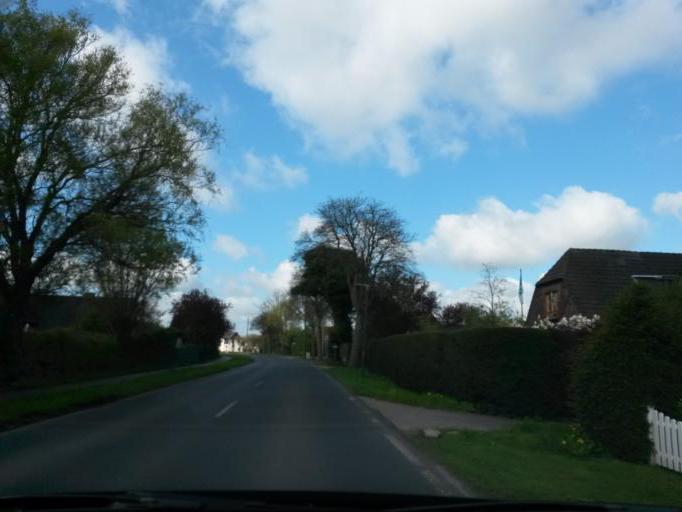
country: DE
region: Schleswig-Holstein
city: Hetlingen
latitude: 53.6094
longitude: 9.6417
